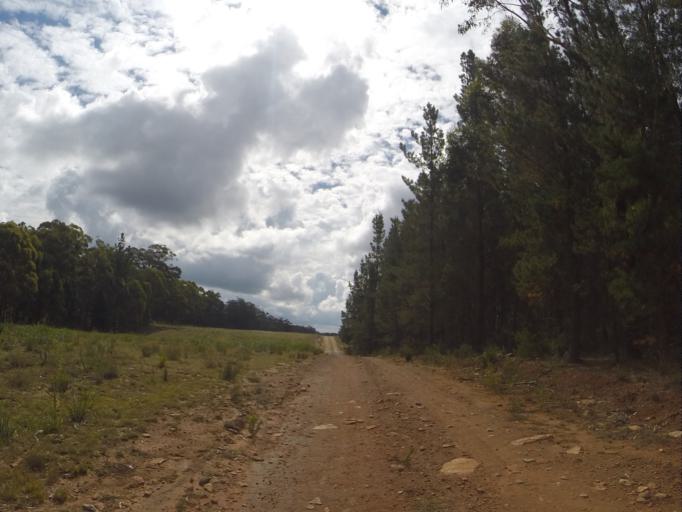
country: AU
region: New South Wales
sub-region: Wingecarribee
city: Moss Vale
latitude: -34.5146
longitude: 150.2271
